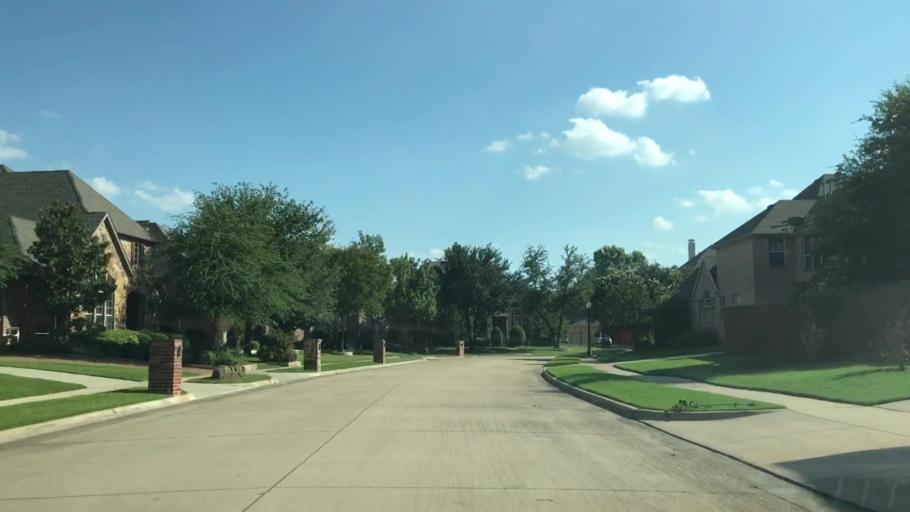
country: US
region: Texas
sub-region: Tarrant County
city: Colleyville
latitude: 32.9194
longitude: -97.1936
